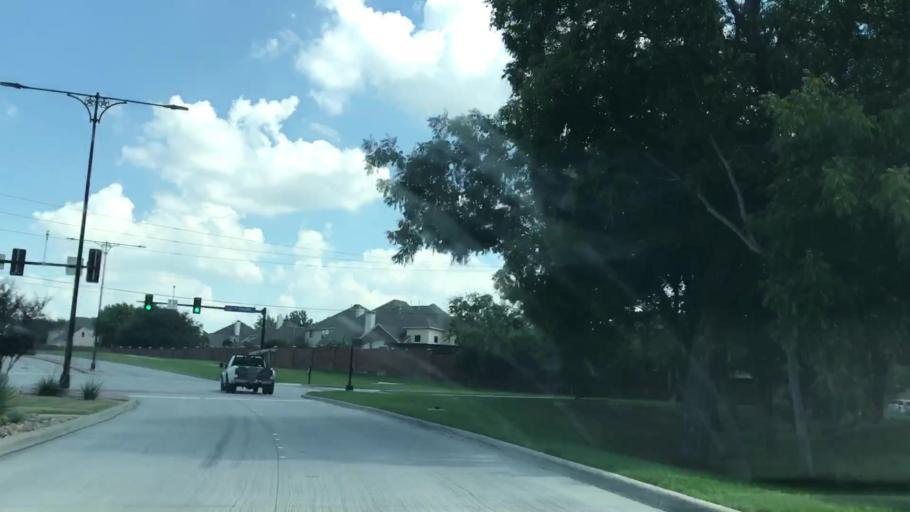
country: US
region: Texas
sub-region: Dallas County
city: Coppell
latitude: 32.9699
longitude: -97.0070
